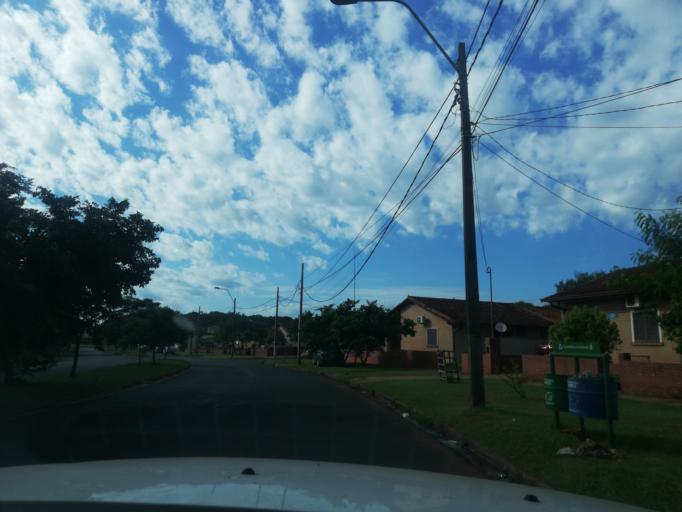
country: PY
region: Itapua
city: Encarnacion
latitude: -27.3539
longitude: -55.8491
